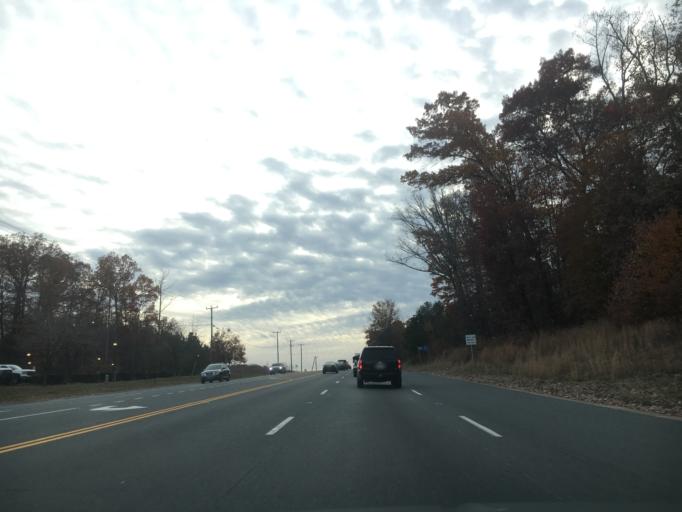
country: US
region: Virginia
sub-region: Stafford County
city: Aquia Harbour
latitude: 38.4733
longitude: -77.3961
